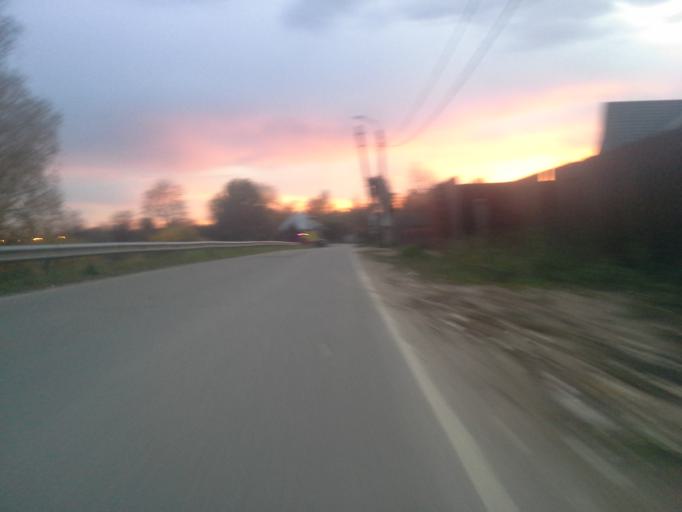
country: RU
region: Moskovskaya
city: Lesnoy Gorodok
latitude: 55.6334
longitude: 37.2259
